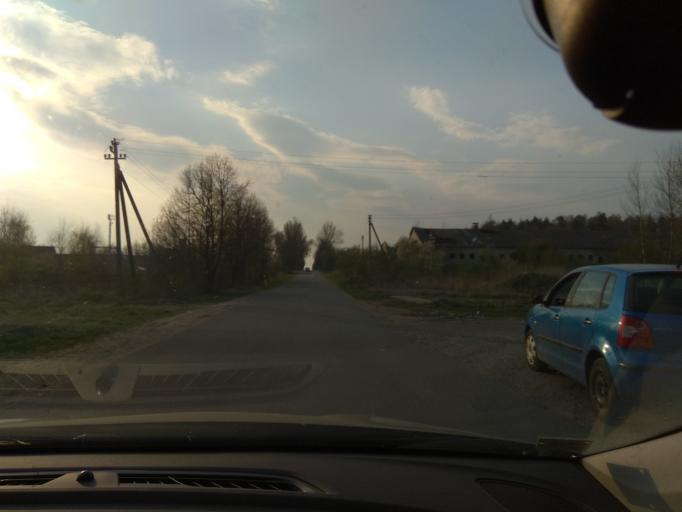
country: LT
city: Baltoji Voke
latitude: 54.5967
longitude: 25.1472
